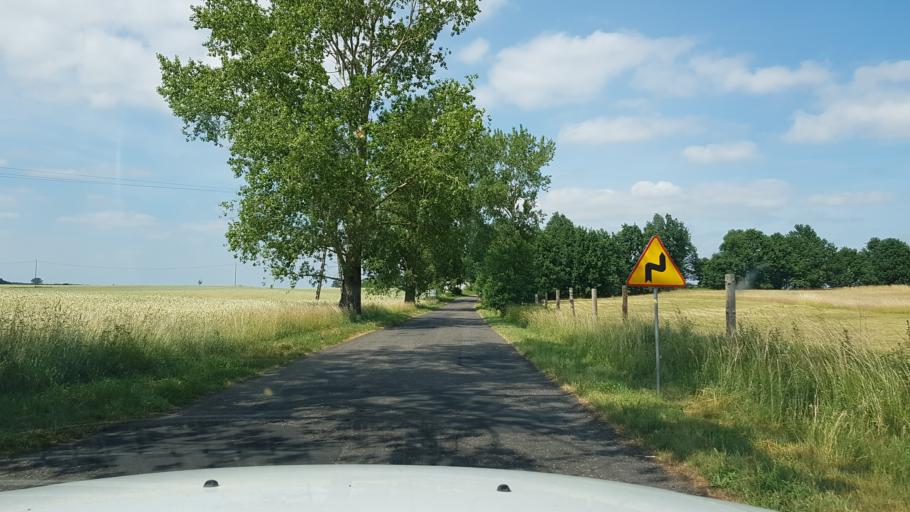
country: PL
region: West Pomeranian Voivodeship
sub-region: Powiat goleniowski
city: Mosty
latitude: 53.5720
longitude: 14.9755
